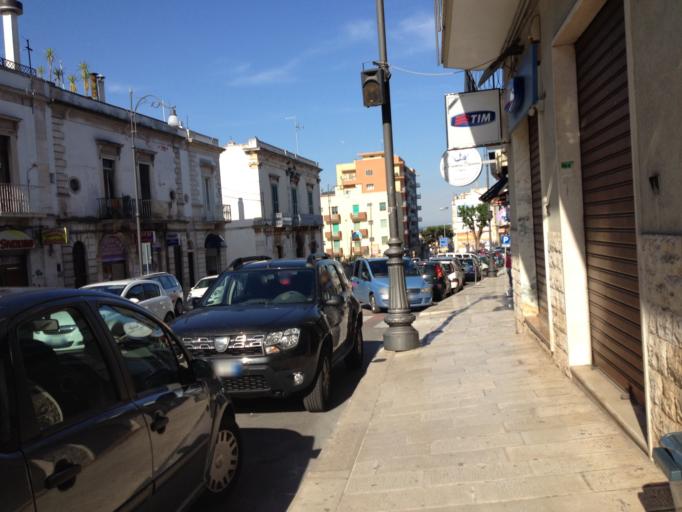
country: IT
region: Apulia
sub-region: Provincia di Bari
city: Putignano
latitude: 40.8480
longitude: 17.1245
